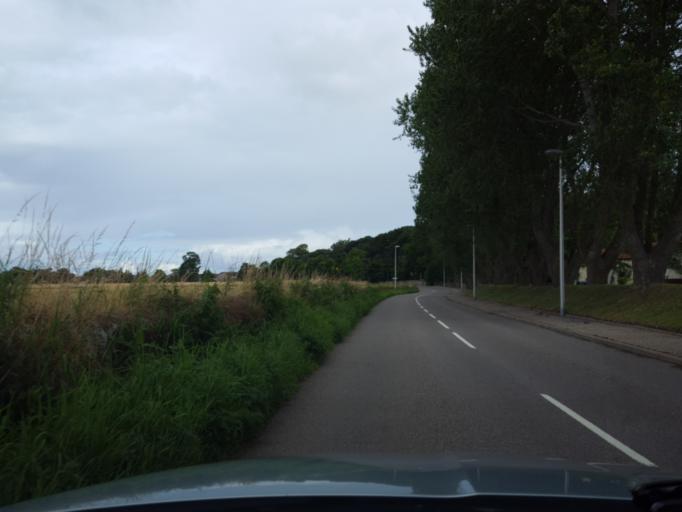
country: GB
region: Scotland
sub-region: Moray
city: Kinloss
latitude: 57.6329
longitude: -3.5609
